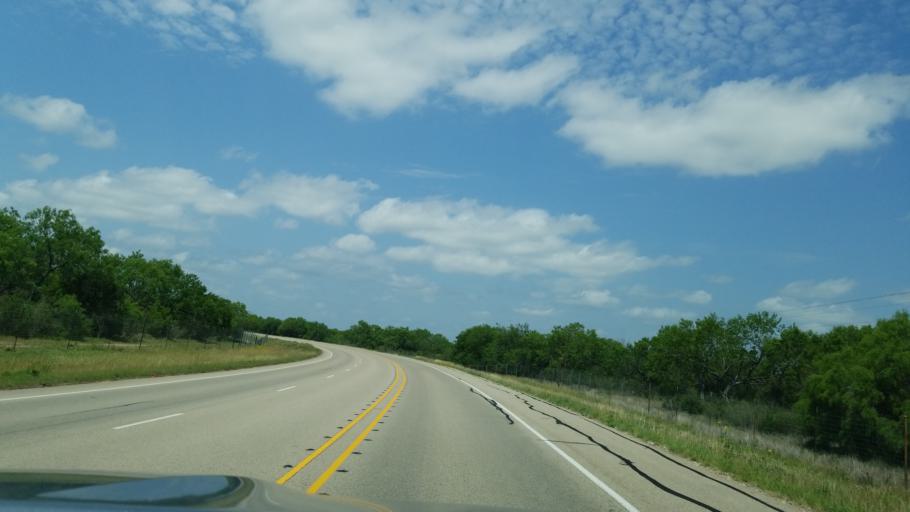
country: US
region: Texas
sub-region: Frio County
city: Pearsall
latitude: 29.0083
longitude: -99.2066
